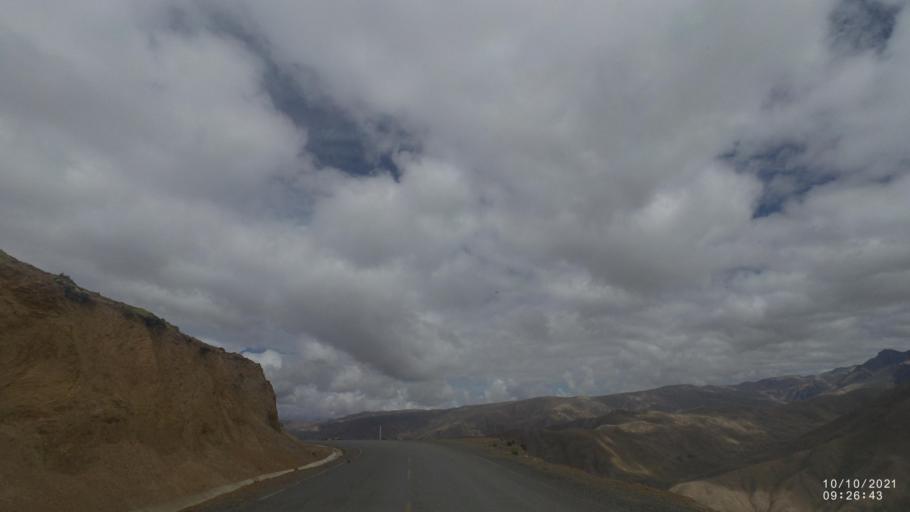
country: BO
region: La Paz
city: Quime
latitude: -17.0956
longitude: -67.3222
